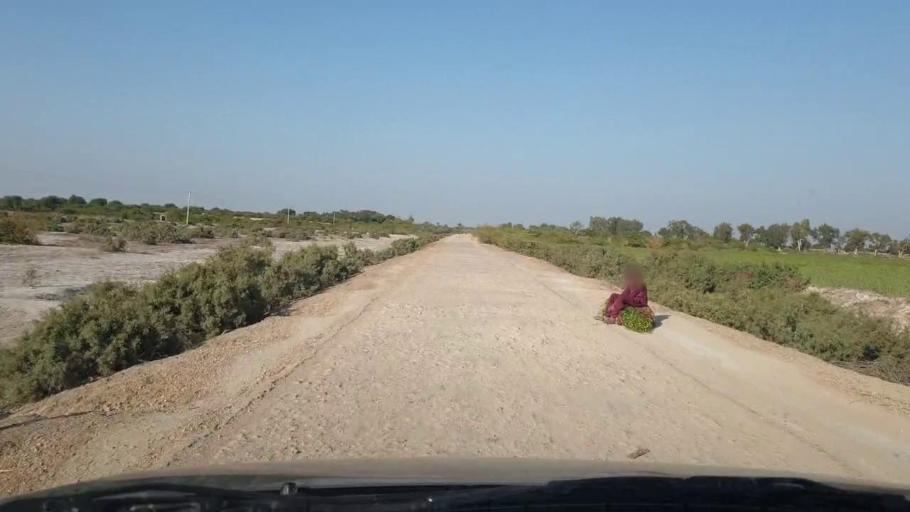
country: PK
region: Sindh
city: Samaro
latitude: 25.1558
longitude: 69.3118
